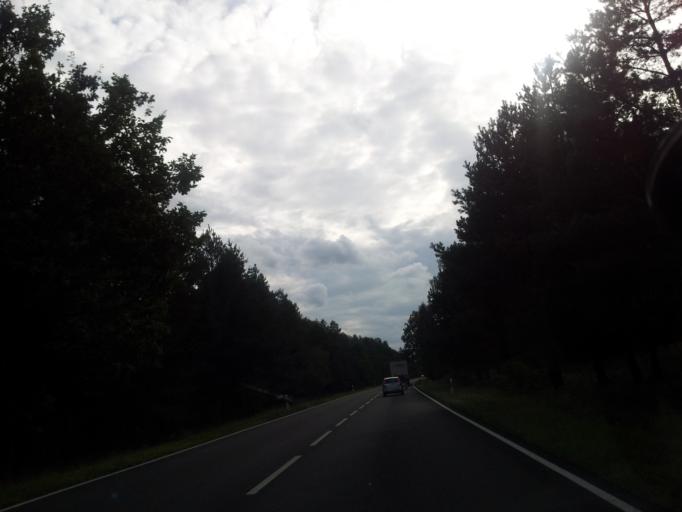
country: DE
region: Saxony-Anhalt
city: Burgstall
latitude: 52.4363
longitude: 11.6422
